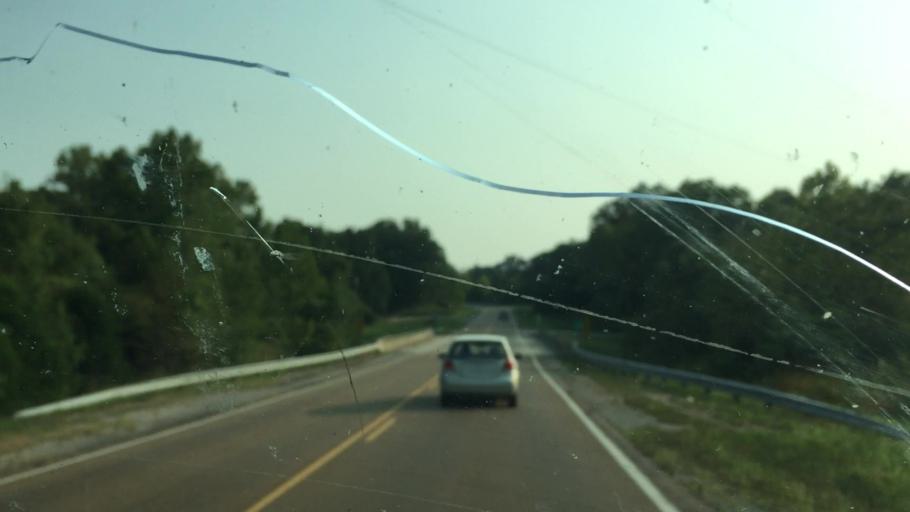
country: US
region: Missouri
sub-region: Pulaski County
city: Richland
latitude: 37.8204
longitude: -92.4057
